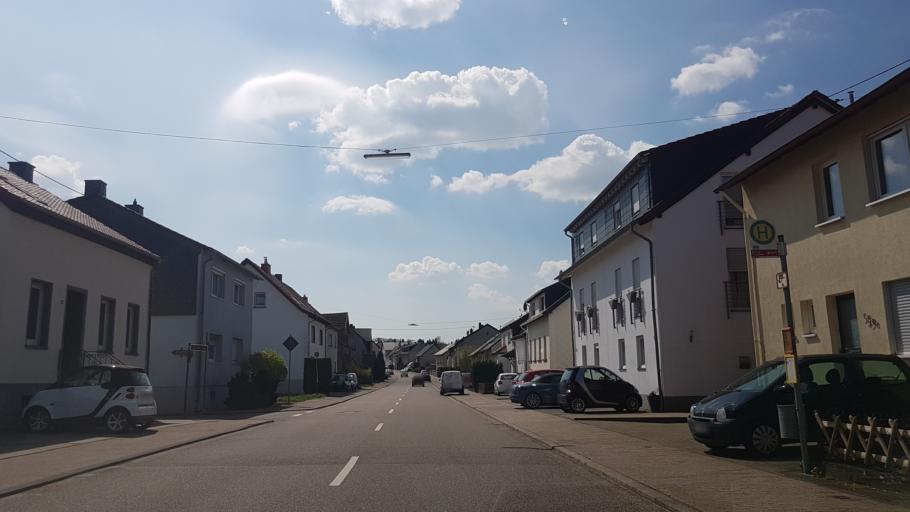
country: DE
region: Saarland
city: Quierschied
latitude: 49.3271
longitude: 6.9939
